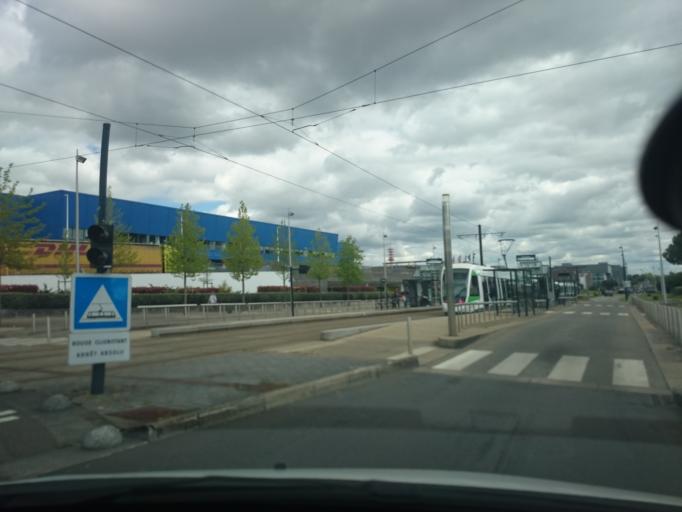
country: FR
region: Pays de la Loire
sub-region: Departement de la Loire-Atlantique
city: Saint-Herblain
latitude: 47.2215
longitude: -1.6333
